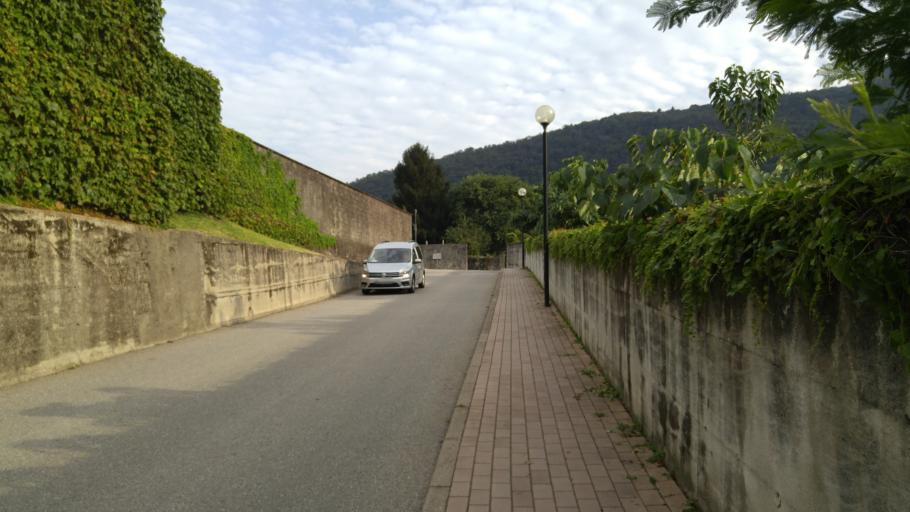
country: IT
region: Piedmont
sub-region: Provincia Verbano-Cusio-Ossola
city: Cannobio
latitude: 46.0633
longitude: 8.6945
